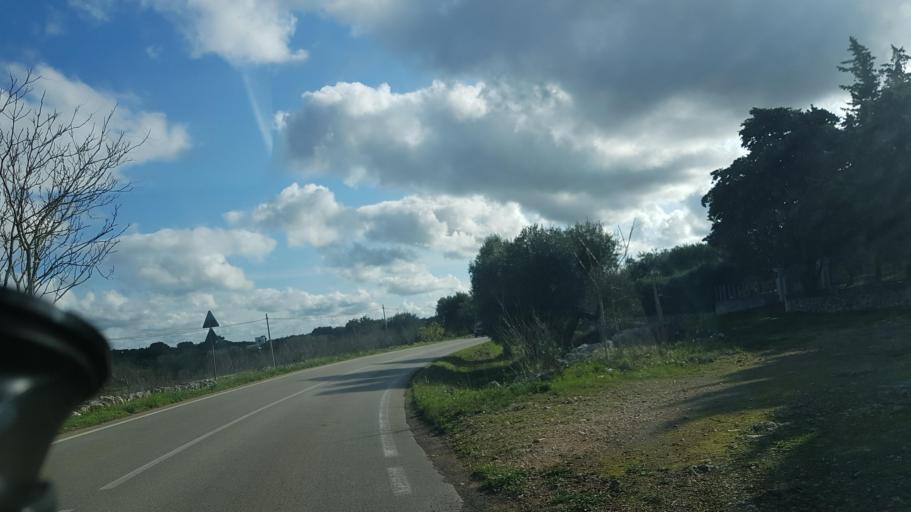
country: IT
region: Apulia
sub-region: Provincia di Brindisi
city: Ostuni
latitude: 40.6846
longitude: 17.5898
